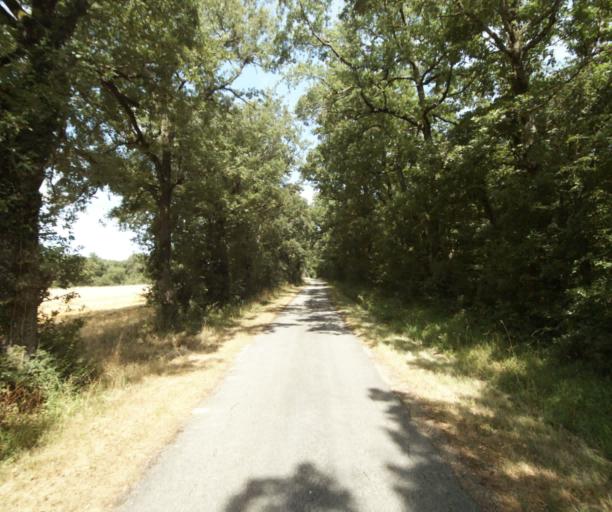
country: FR
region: Midi-Pyrenees
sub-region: Departement du Tarn
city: Dourgne
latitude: 43.4845
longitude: 2.1111
